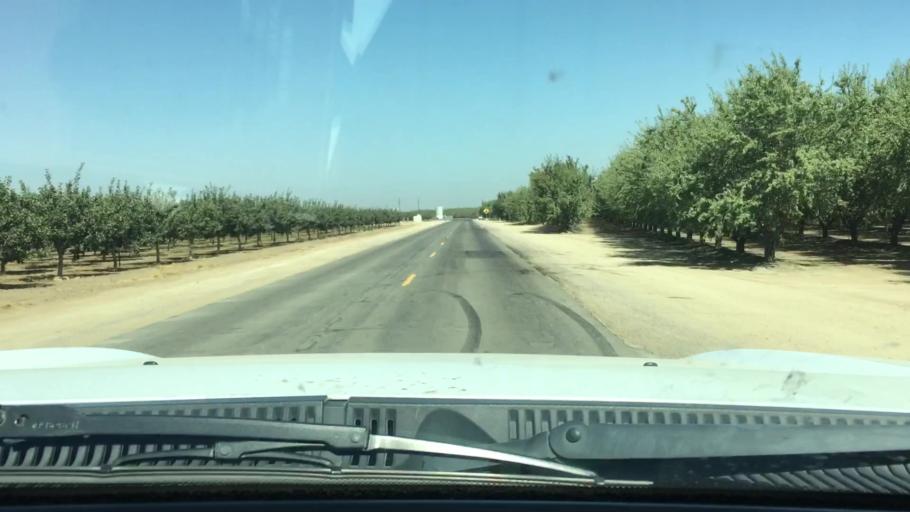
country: US
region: California
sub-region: Kern County
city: Shafter
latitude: 35.5544
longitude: -119.2770
